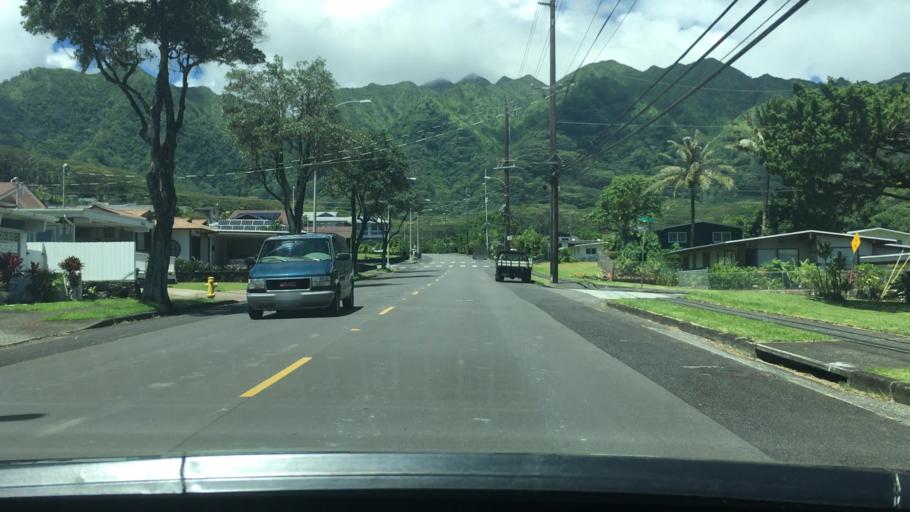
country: US
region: Hawaii
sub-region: Honolulu County
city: Honolulu
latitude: 21.3226
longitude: -157.8040
